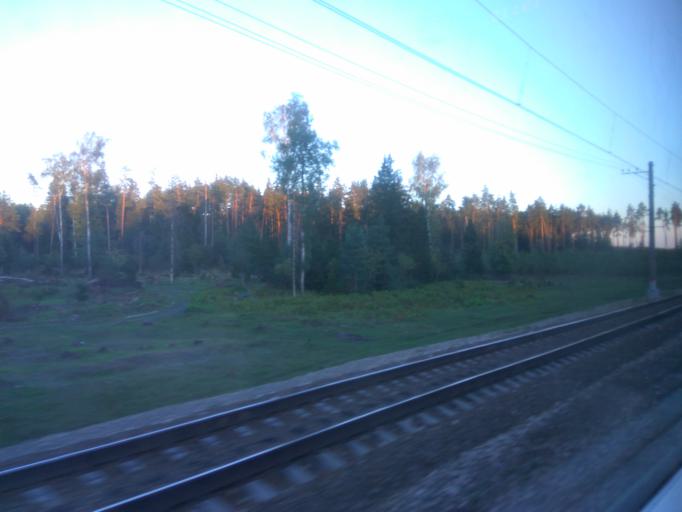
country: RU
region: Moskovskaya
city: Fryazevo
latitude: 55.7438
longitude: 38.4794
